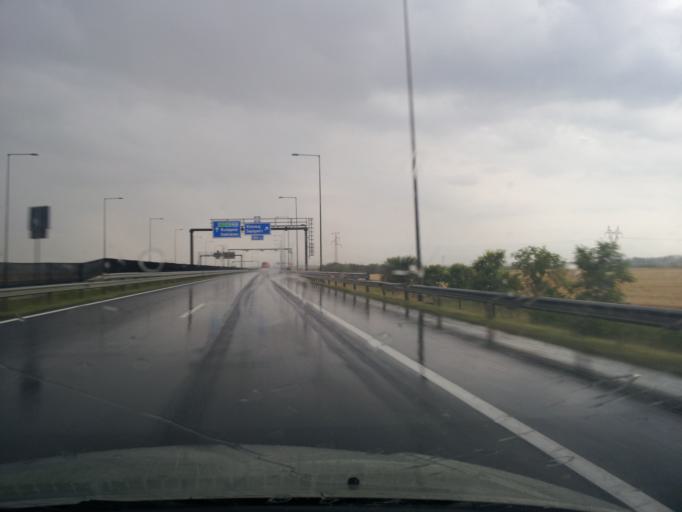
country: HU
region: Borsod-Abauj-Zemplen
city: Alsozsolca
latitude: 48.0517
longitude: 20.8508
